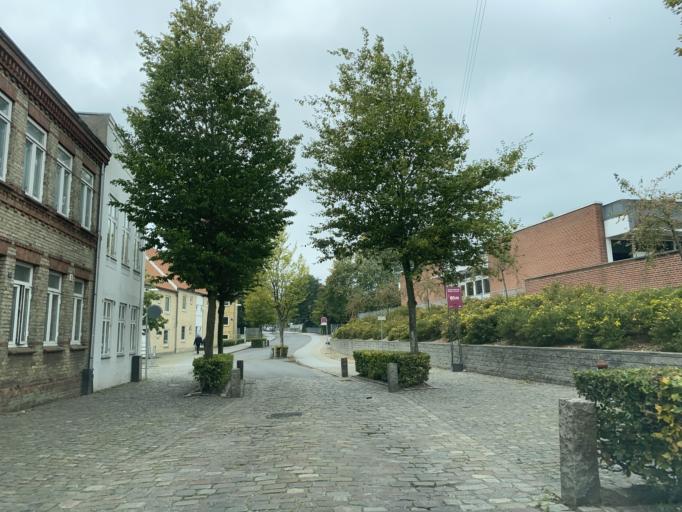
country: DK
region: South Denmark
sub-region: Haderslev Kommune
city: Haderslev
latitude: 55.2537
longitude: 9.4766
